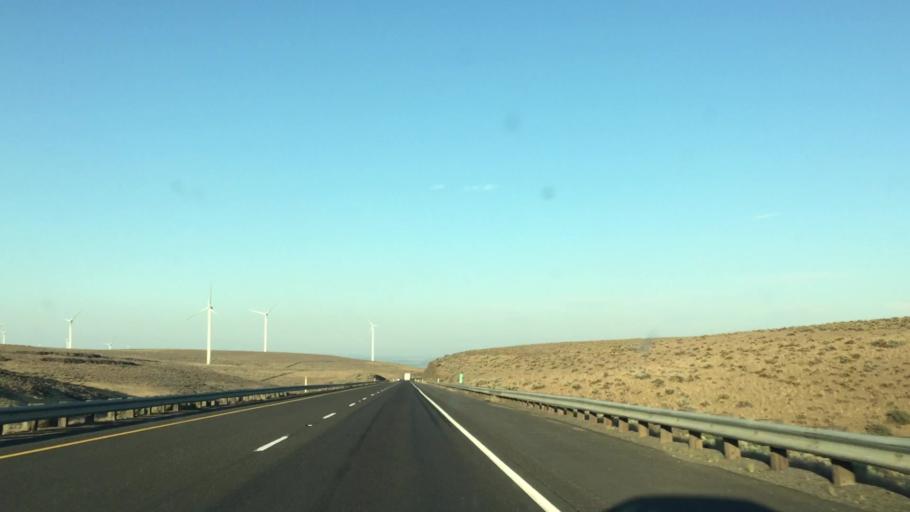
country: US
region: Washington
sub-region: Kittitas County
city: Kittitas
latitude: 46.9438
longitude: -120.1601
